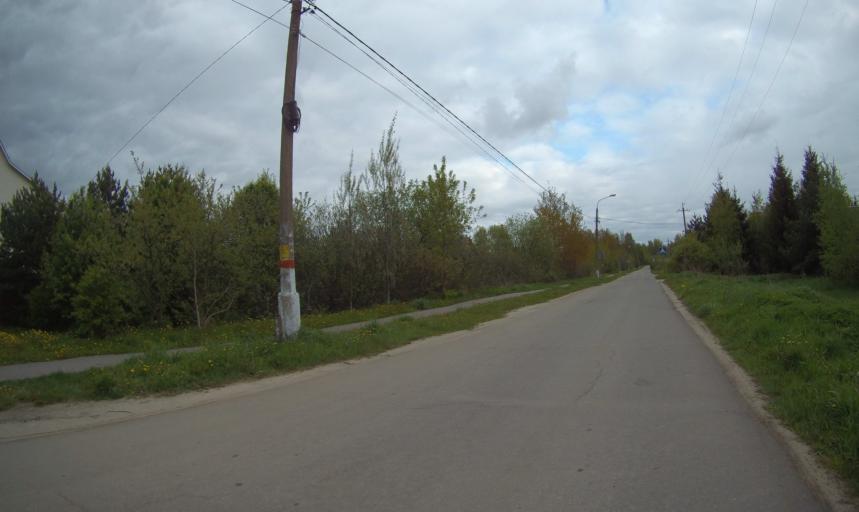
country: RU
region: Moskovskaya
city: Rechitsy
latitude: 55.6096
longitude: 38.5409
